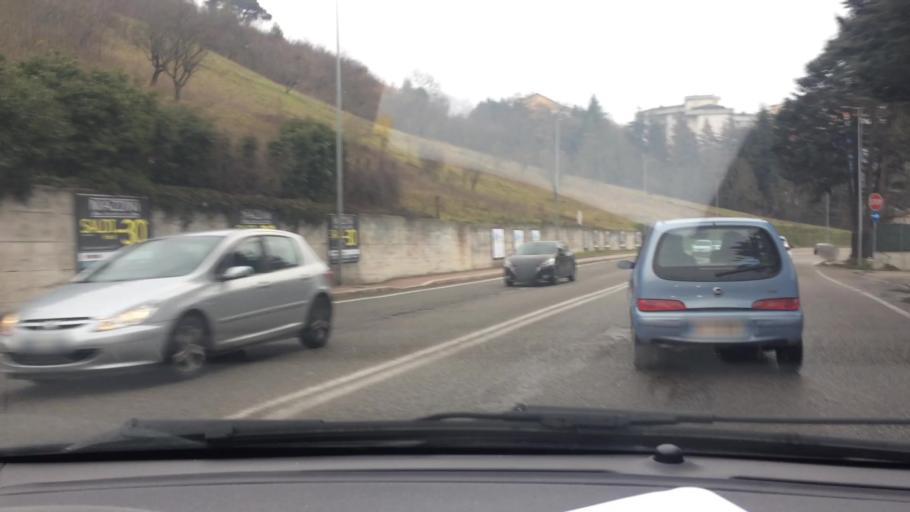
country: IT
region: Basilicate
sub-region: Provincia di Potenza
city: Potenza
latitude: 40.6316
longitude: 15.7956
